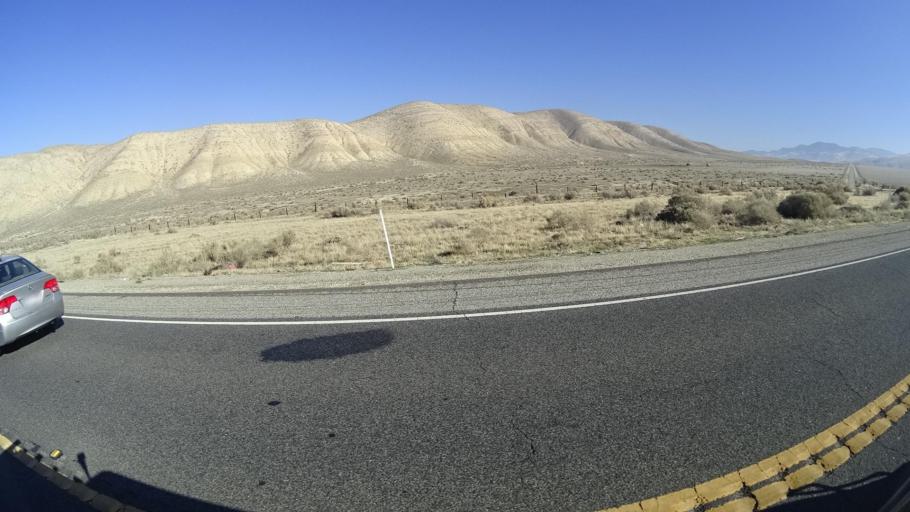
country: US
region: California
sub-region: Kern County
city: Maricopa
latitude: 35.0052
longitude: -119.4098
